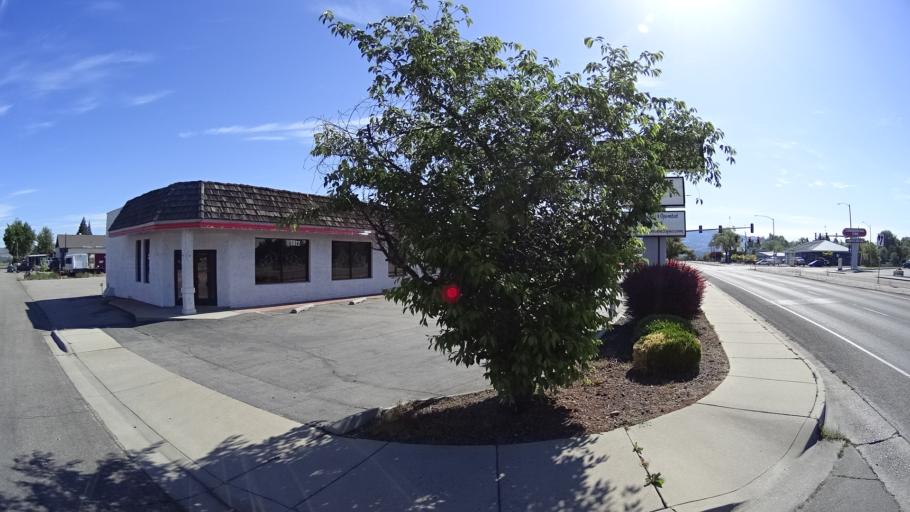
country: US
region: Idaho
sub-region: Ada County
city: Garden City
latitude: 43.6191
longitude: -116.2447
